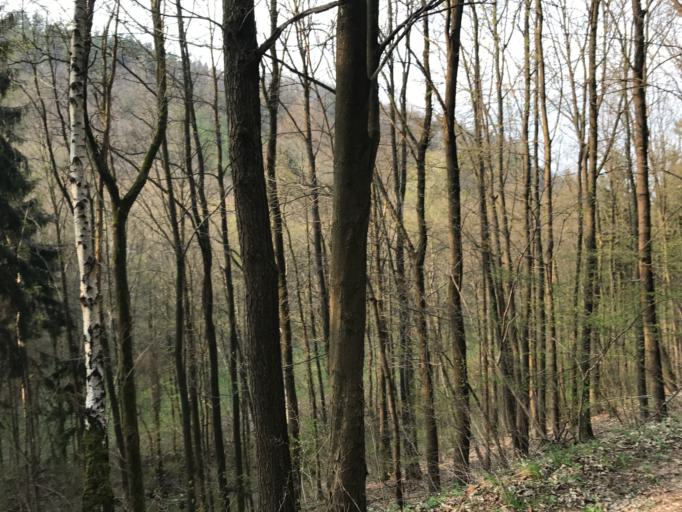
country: DE
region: Thuringia
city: Saalfeld
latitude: 50.6328
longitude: 11.3374
